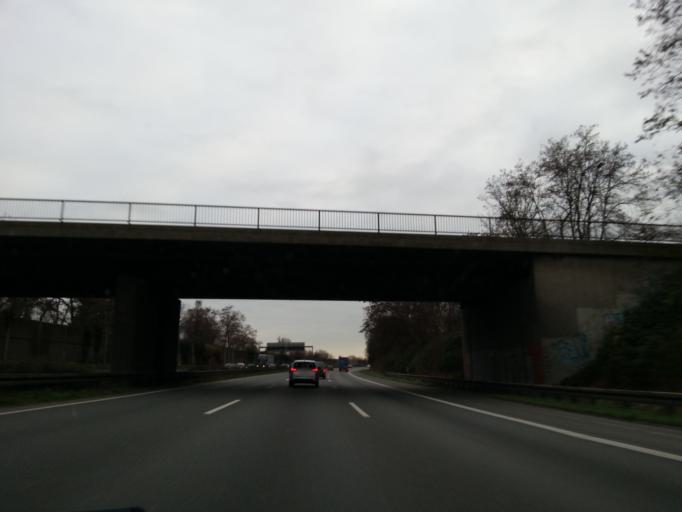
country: DE
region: North Rhine-Westphalia
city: Meiderich
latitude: 51.4675
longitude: 6.8161
